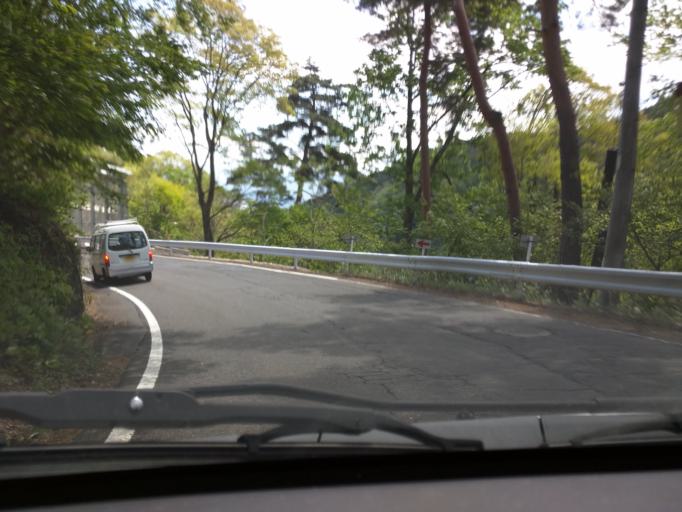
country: JP
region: Nagano
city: Nagano-shi
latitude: 36.6741
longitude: 138.1735
